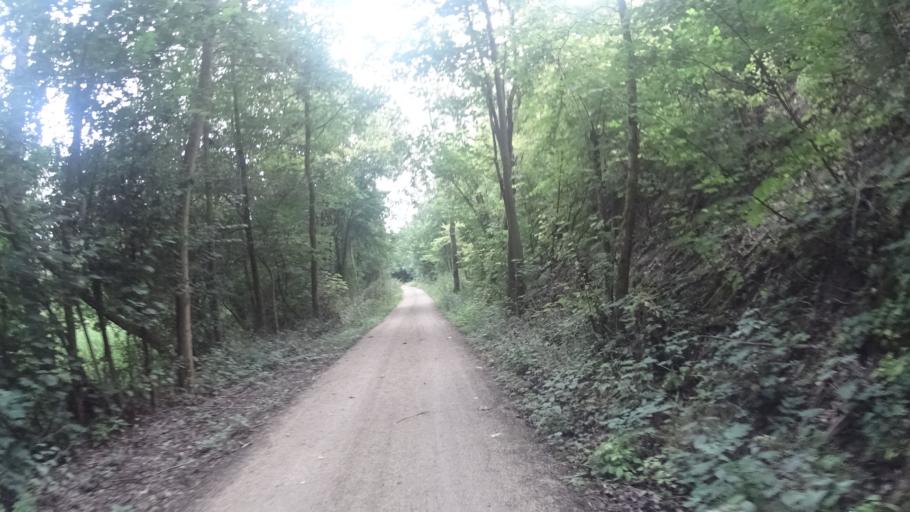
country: FR
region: Picardie
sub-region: Departement de l'Aisne
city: Origny-Sainte-Benoite
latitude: 49.8708
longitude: 3.5281
